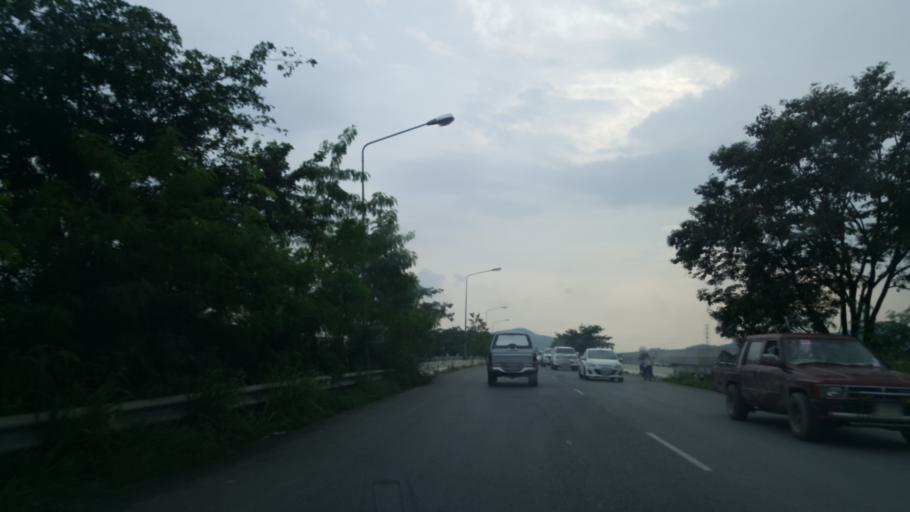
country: TH
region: Rayong
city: Ban Chang
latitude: 12.7332
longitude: 100.9867
